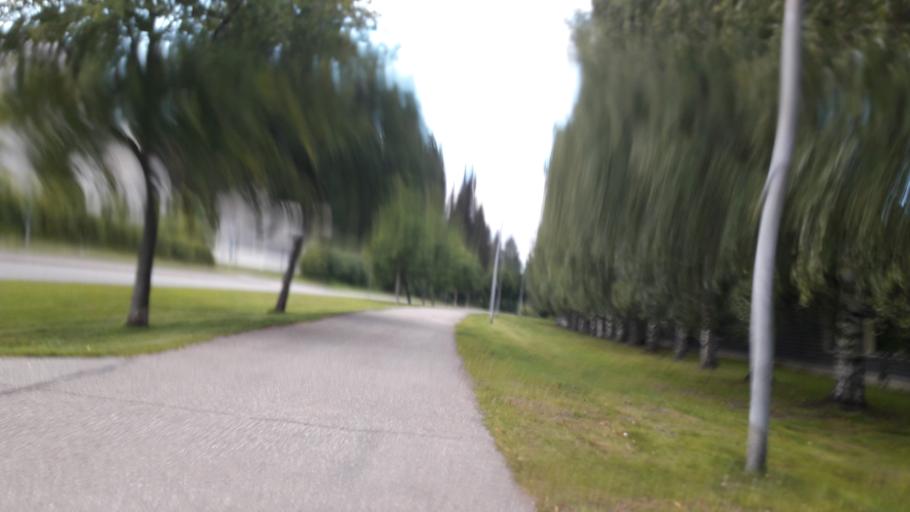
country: FI
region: North Karelia
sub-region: Joensuu
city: Joensuu
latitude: 62.5887
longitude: 29.8072
